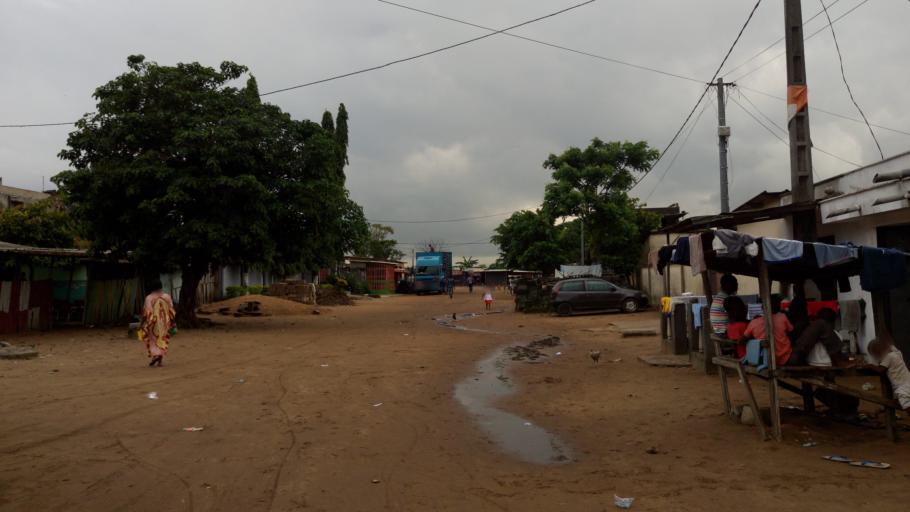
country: CI
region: Lagunes
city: Abobo
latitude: 5.4089
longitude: -3.9971
